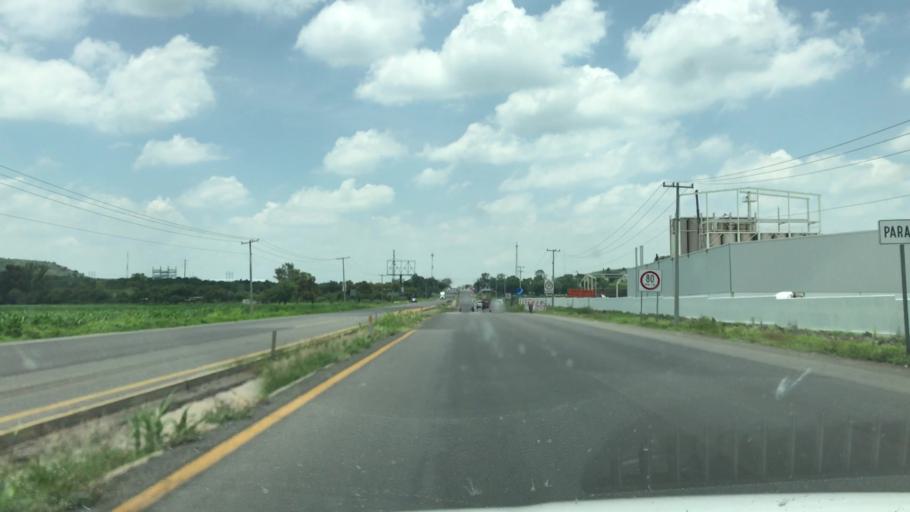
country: MX
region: Guanajuato
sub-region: Irapuato
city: San Ignacio de Rivera (Ojo de Agua)
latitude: 20.5527
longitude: -101.4521
